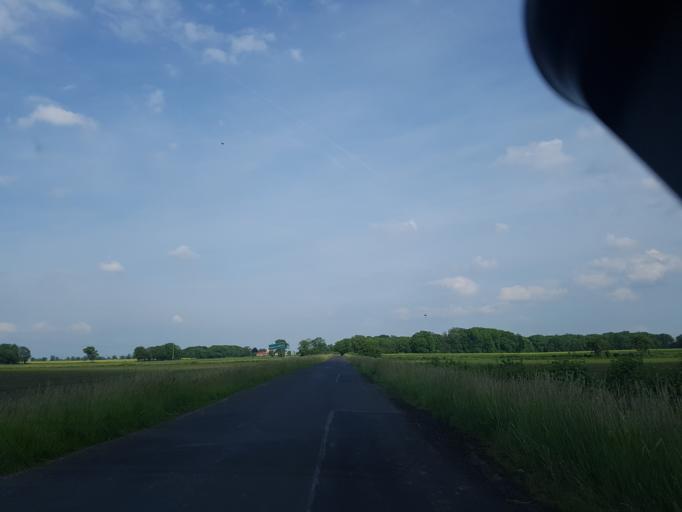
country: PL
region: Lower Silesian Voivodeship
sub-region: Powiat wroclawski
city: Zorawina
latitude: 50.9107
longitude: 17.0706
